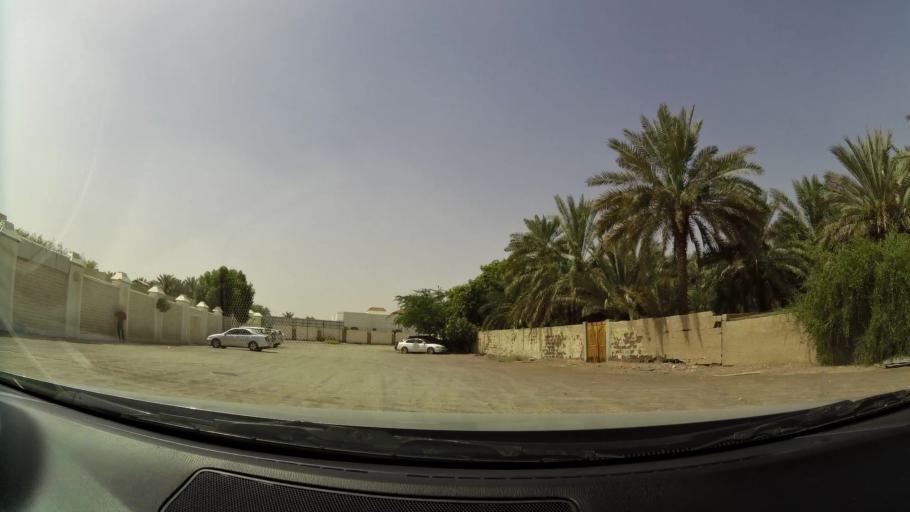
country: AE
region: Abu Dhabi
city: Al Ain
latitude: 24.2285
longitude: 55.7083
